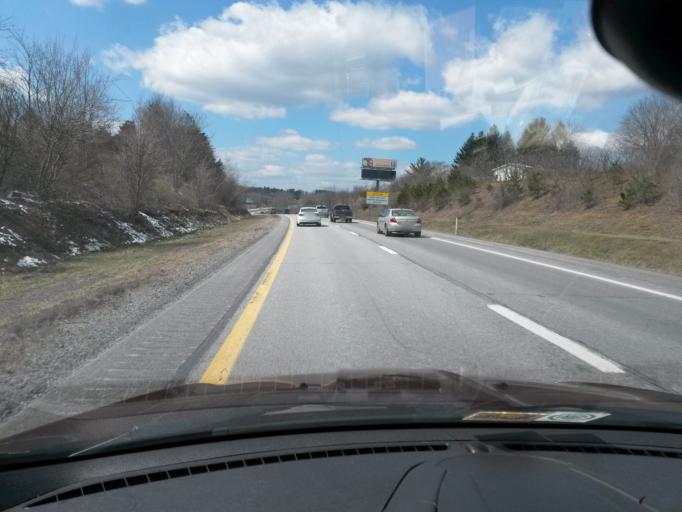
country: US
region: West Virginia
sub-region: Mercer County
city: Athens
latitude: 37.3825
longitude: -81.0474
